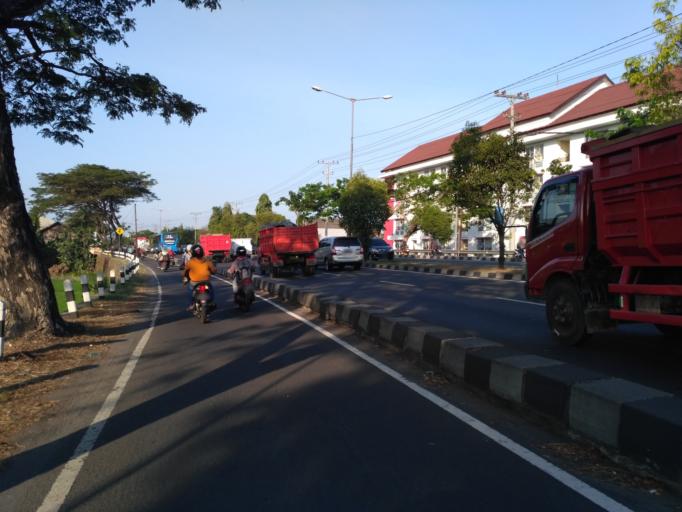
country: ID
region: Daerah Istimewa Yogyakarta
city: Sewon
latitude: -7.8364
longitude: 110.3761
